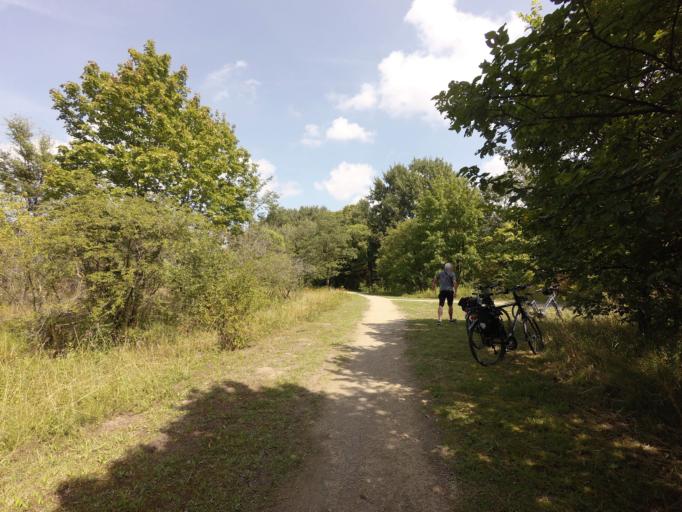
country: NL
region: South Holland
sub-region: Gemeente Sliedrecht
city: Sliedrecht
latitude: 51.7650
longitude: 4.7791
